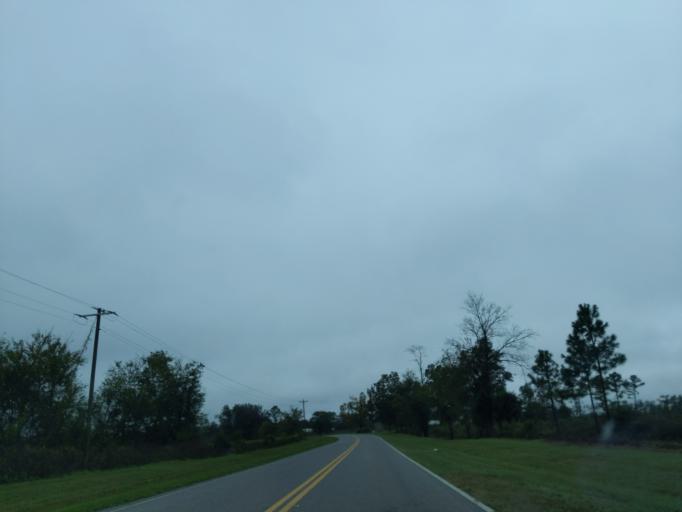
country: US
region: Florida
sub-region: Jackson County
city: Sneads
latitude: 30.6781
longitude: -84.9339
